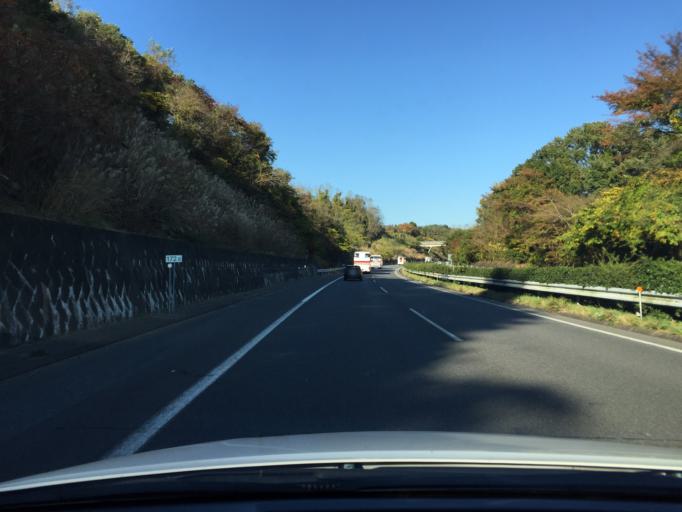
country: JP
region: Fukushima
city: Iwaki
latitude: 37.0491
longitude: 140.8216
